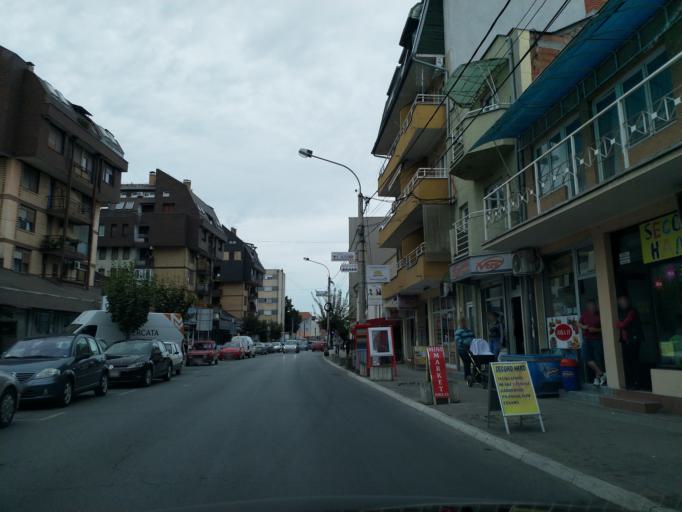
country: RS
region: Central Serbia
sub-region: Pomoravski Okrug
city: Jagodina
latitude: 43.9814
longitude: 21.2563
